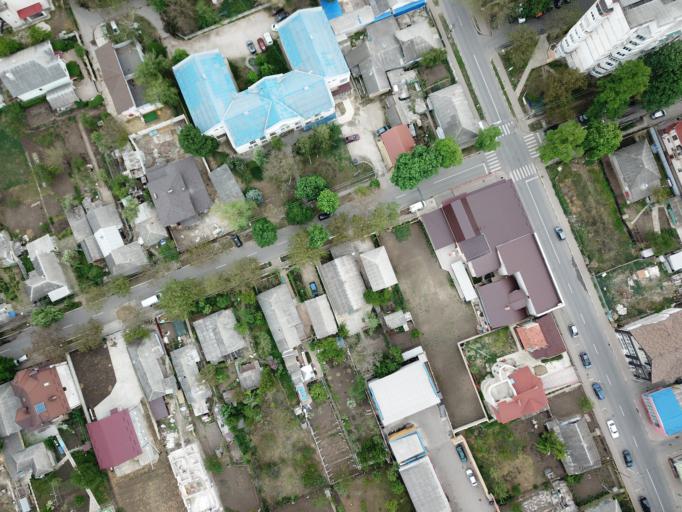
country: MD
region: Ungheni
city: Ungheni
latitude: 47.2091
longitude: 27.7985
